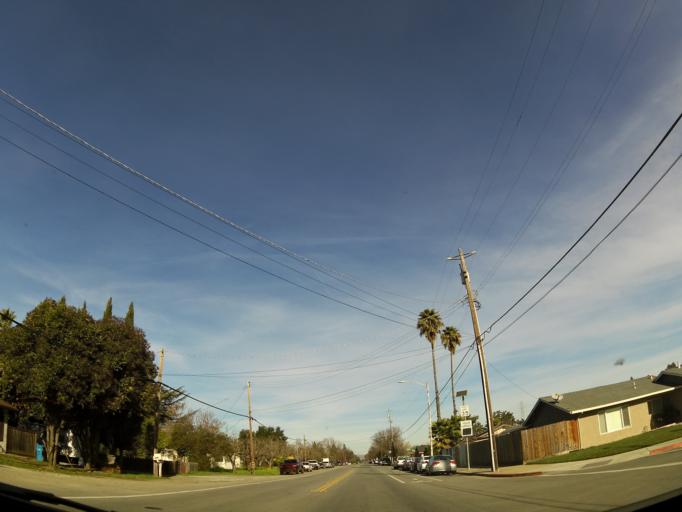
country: US
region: California
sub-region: Santa Clara County
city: Gilroy
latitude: 37.0230
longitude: -121.5701
